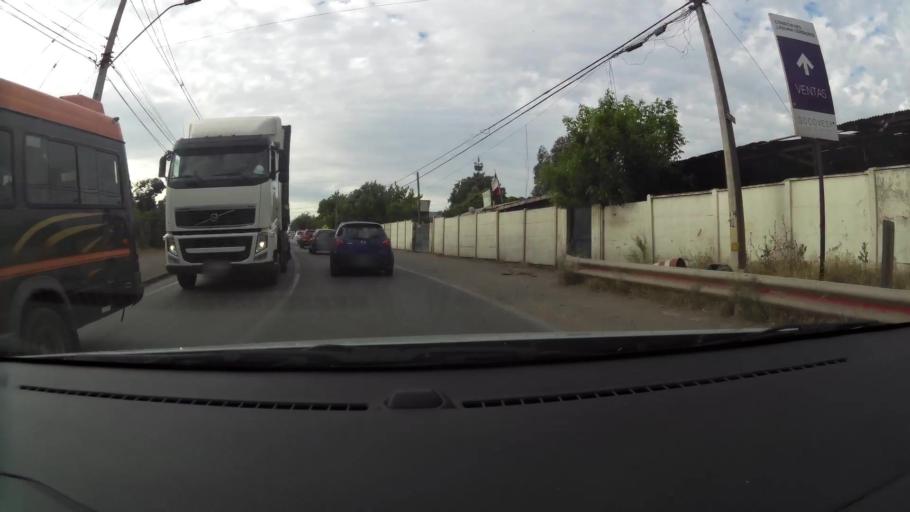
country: CL
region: Santiago Metropolitan
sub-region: Provincia de Maipo
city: San Bernardo
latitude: -33.6495
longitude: -70.6625
